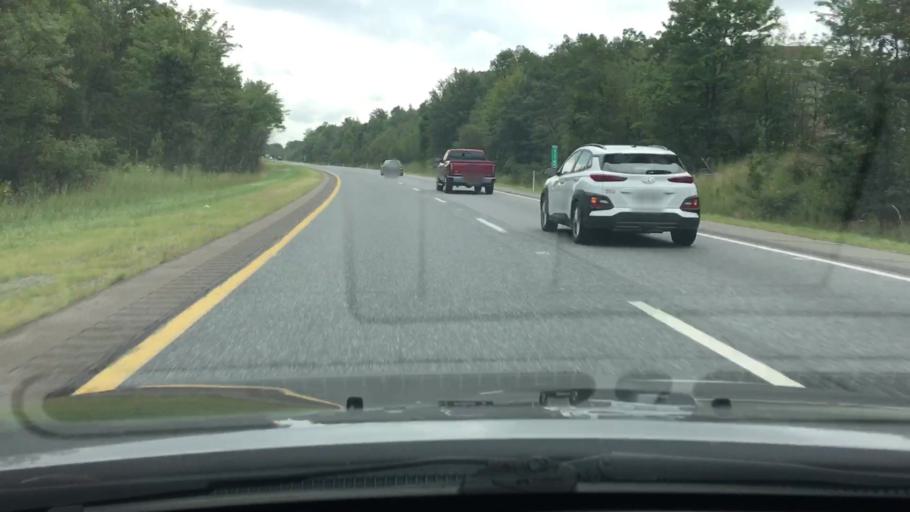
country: US
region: Pennsylvania
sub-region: Schuylkill County
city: Ashland
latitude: 40.7086
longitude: -76.3601
